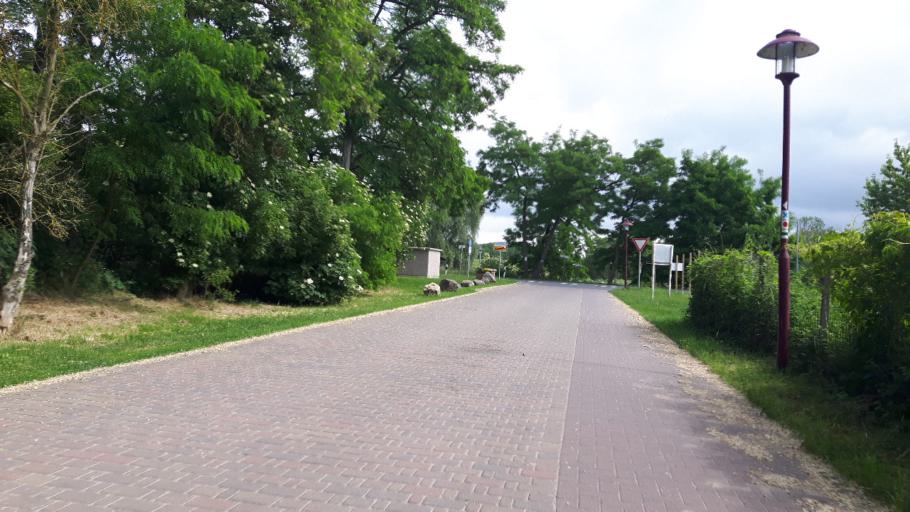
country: DE
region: Brandenburg
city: Mescherin
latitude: 53.2580
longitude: 14.4372
